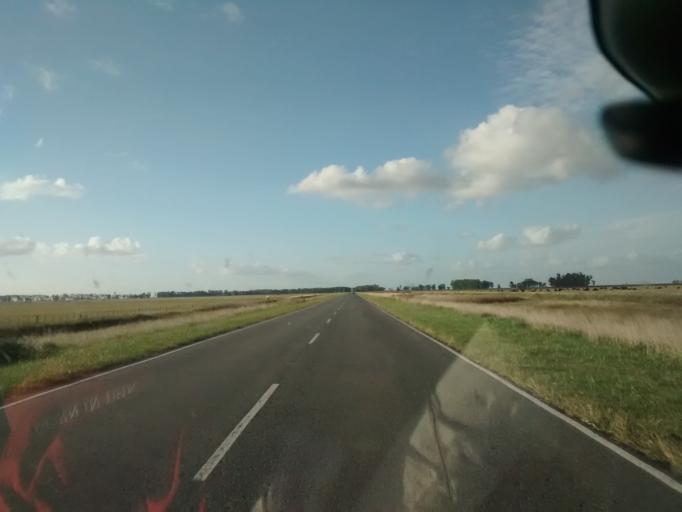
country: AR
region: Buenos Aires
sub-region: Partido de General Belgrano
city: General Belgrano
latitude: -36.1726
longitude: -58.5940
